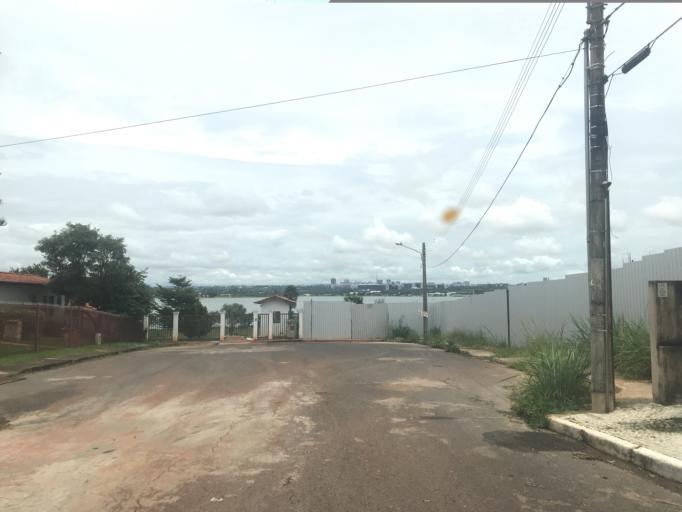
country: BR
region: Federal District
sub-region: Brasilia
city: Brasilia
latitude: -15.8378
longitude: -47.8391
